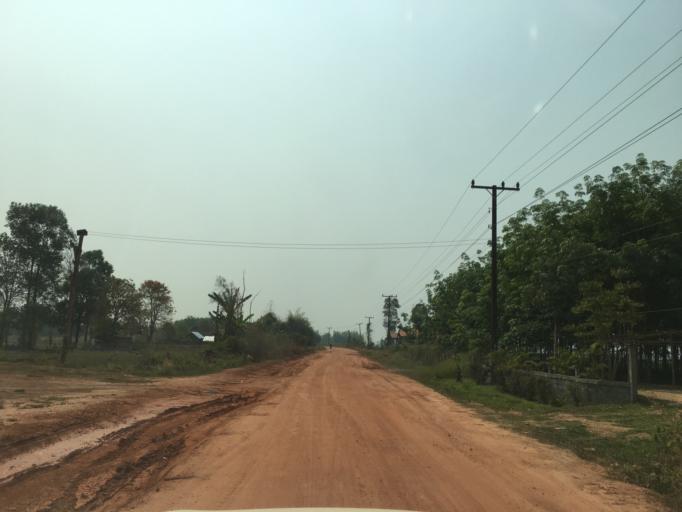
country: LA
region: Bolikhamxai
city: Ban Nahin
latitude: 18.2017
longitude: 104.0757
